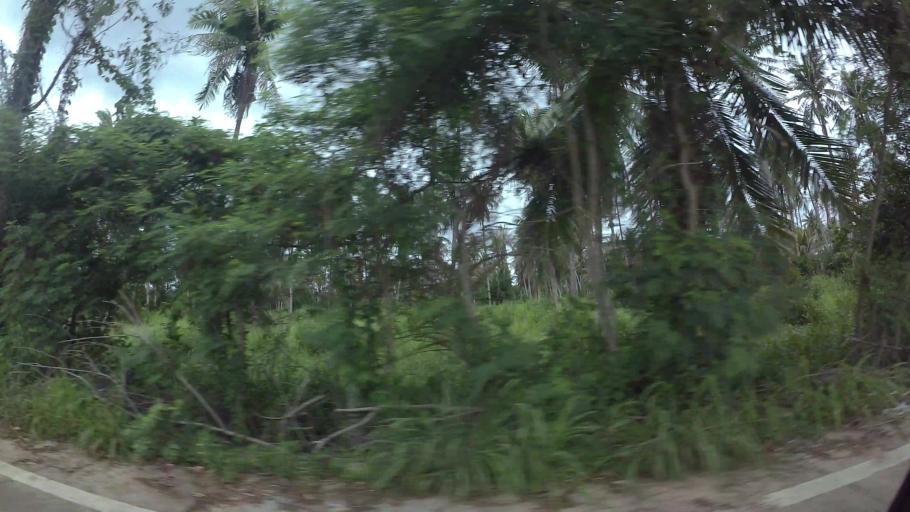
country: TH
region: Chon Buri
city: Si Racha
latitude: 13.1764
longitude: 100.9794
